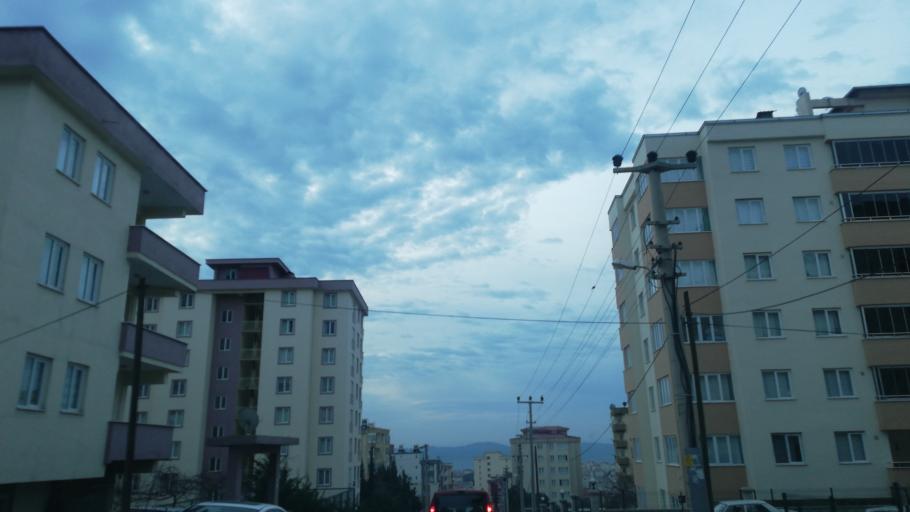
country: TR
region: Kahramanmaras
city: Kahramanmaras
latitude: 37.5967
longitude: 36.8988
